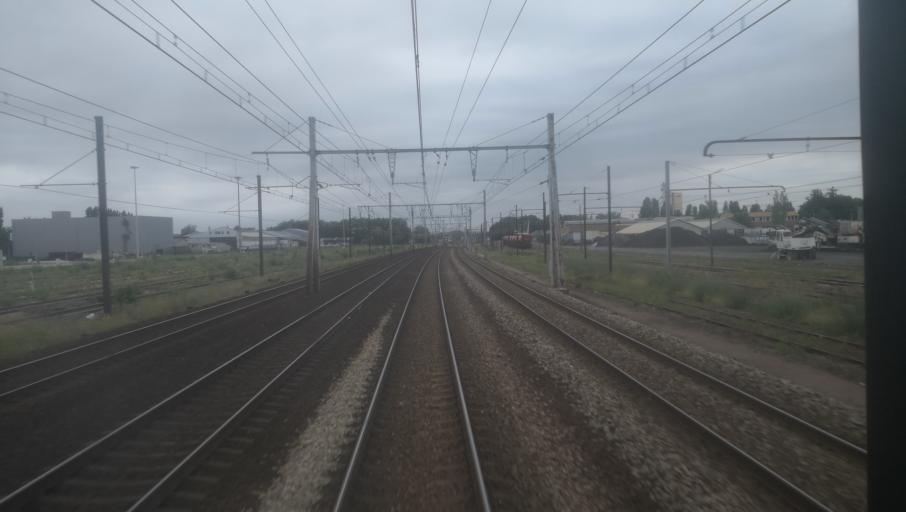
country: FR
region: Ile-de-France
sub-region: Departement de l'Essonne
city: Marolles-en-Hurepoix
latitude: 48.5816
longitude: 2.2902
